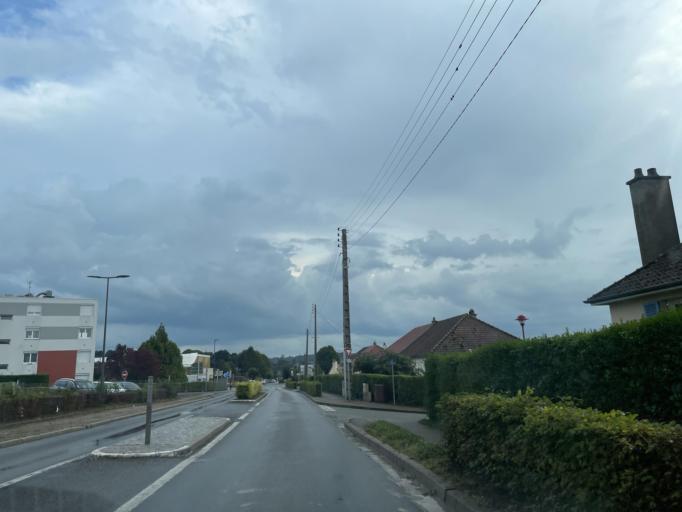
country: FR
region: Haute-Normandie
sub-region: Departement de la Seine-Maritime
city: Neufchatel-en-Bray
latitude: 49.7388
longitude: 1.4383
